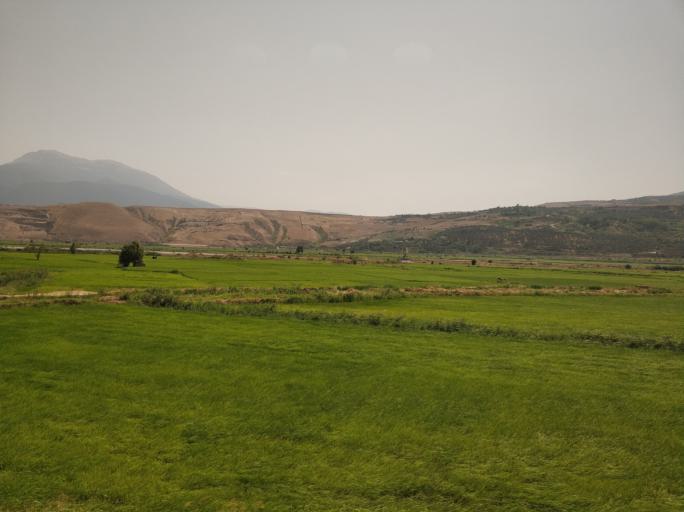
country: IR
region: Gilan
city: Pa'in-e Bazar-e Rudbar
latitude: 36.8810
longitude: 49.4976
